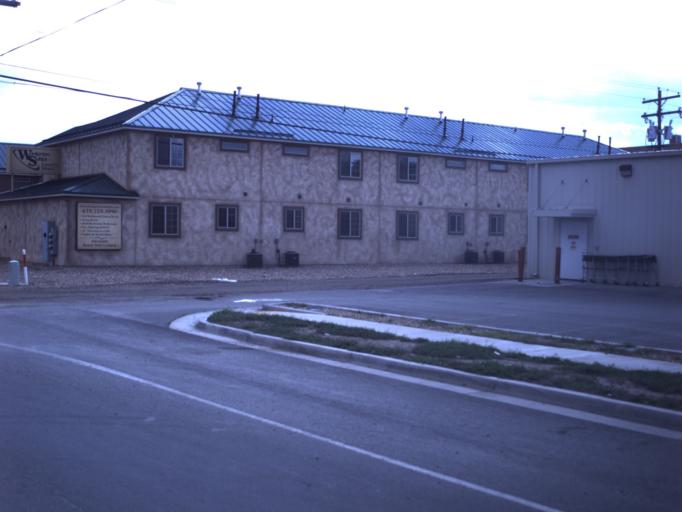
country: US
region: Utah
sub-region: Duchesne County
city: Duchesne
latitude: 40.1631
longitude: -110.4031
